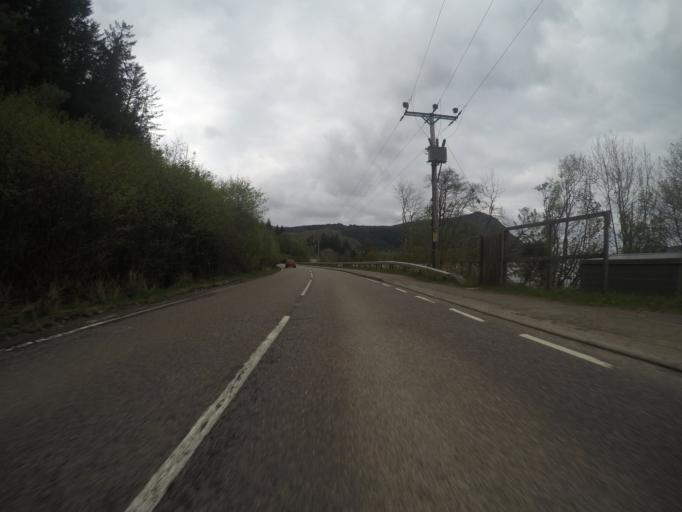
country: GB
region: Scotland
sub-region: Highland
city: Beauly
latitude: 57.2031
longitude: -4.6080
